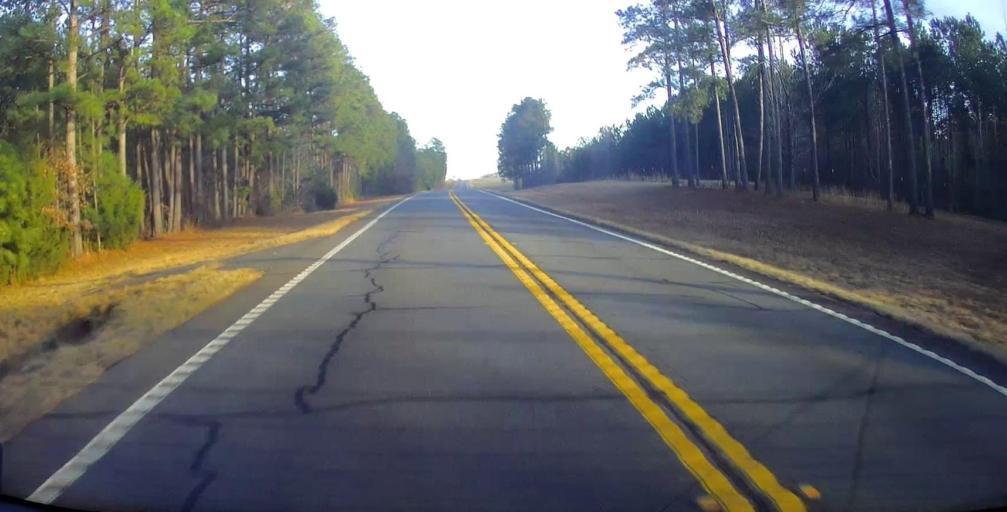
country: US
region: Georgia
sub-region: Talbot County
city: Sardis
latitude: 32.7893
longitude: -84.5337
